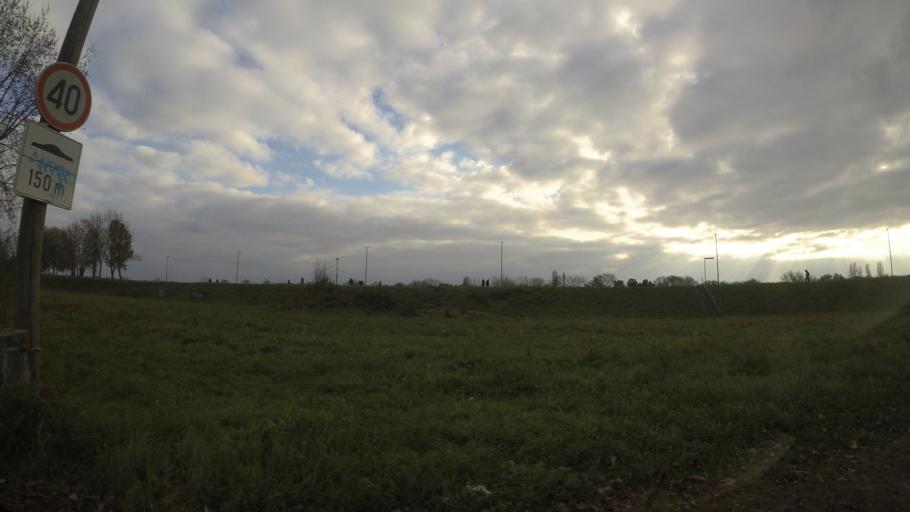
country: HR
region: Grad Zagreb
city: Novi Zagreb
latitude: 45.7905
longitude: 15.9874
